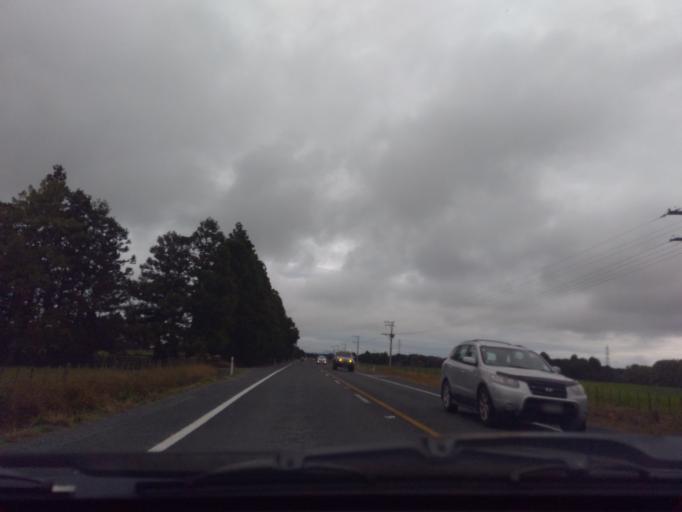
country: NZ
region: Northland
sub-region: Whangarei
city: Ruakaka
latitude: -35.9970
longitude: 174.4182
